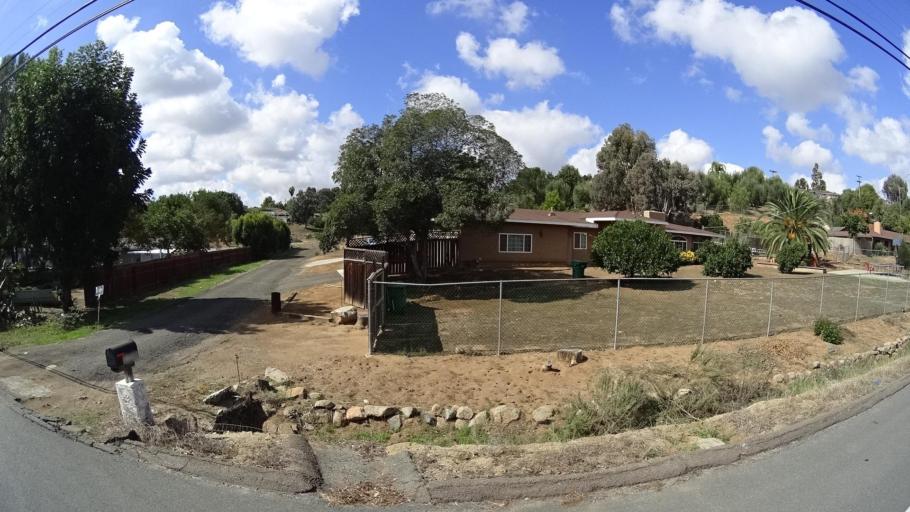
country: US
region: California
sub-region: San Diego County
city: Rancho San Diego
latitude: 32.7649
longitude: -116.9414
